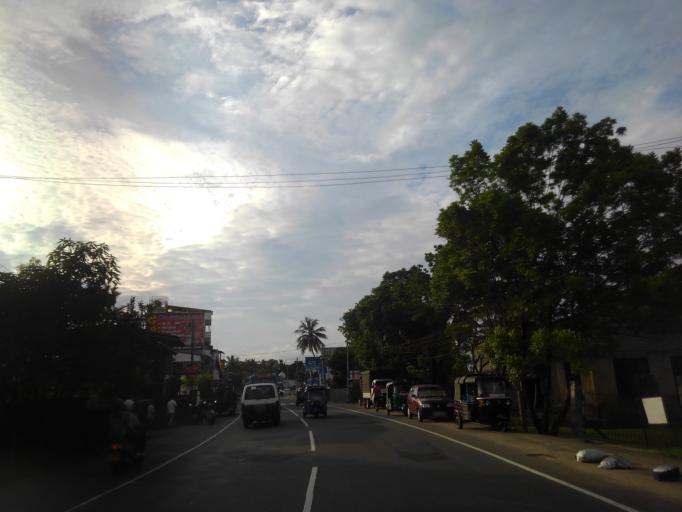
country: LK
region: Southern
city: Galle
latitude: 6.0350
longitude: 80.2335
